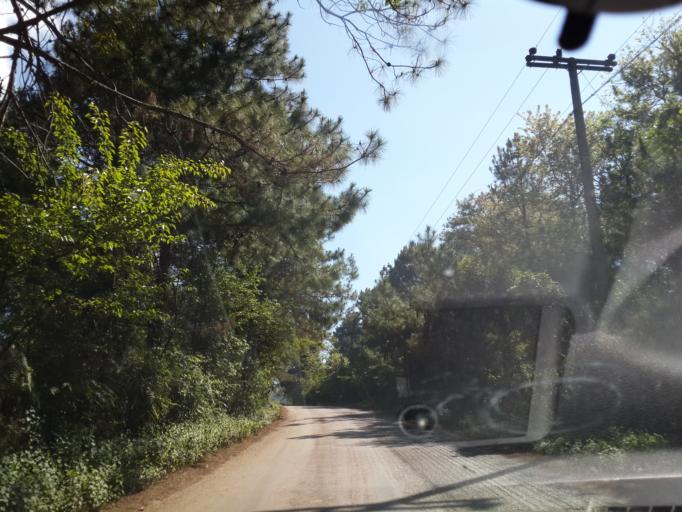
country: TH
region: Chiang Mai
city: Fang
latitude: 19.9217
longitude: 99.0475
